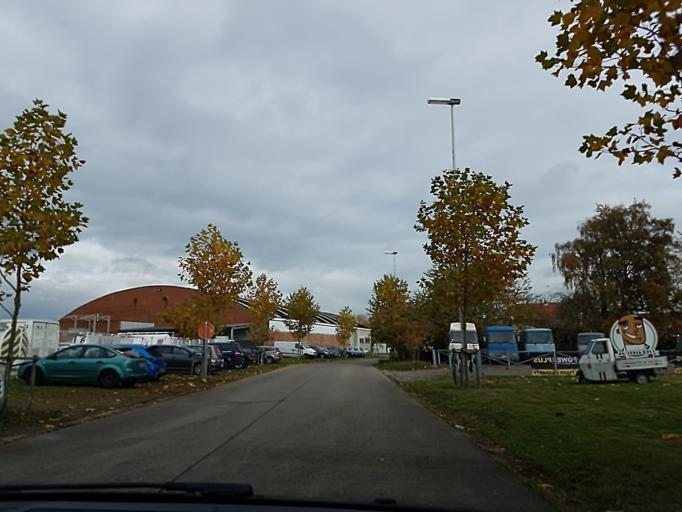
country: BE
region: Flanders
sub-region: Provincie Antwerpen
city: Lier
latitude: 51.1497
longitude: 4.5598
